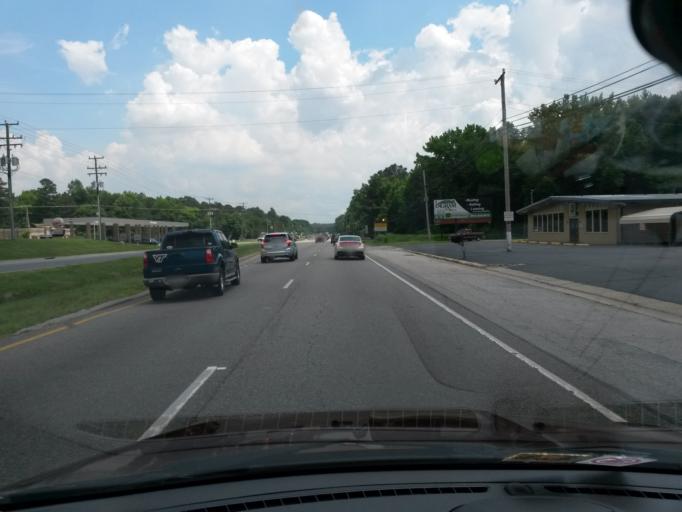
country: US
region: Virginia
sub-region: Chesterfield County
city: Enon
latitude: 37.3357
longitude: -77.3280
